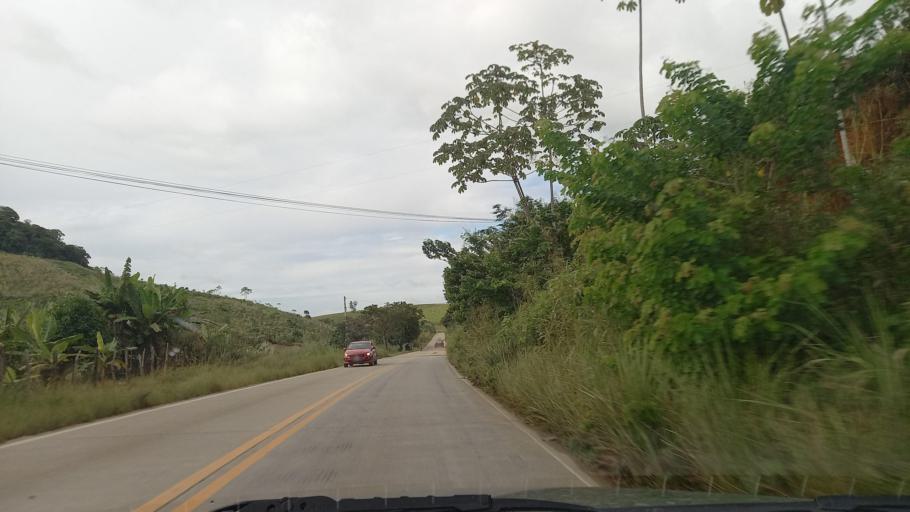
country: BR
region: Pernambuco
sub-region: Maraial
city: Maraial
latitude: -8.7605
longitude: -35.8553
